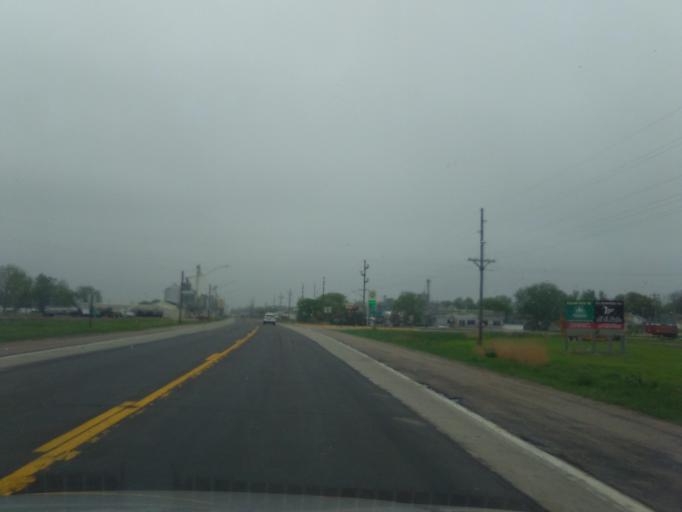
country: US
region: Nebraska
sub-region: Cuming County
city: Wisner
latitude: 41.9251
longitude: -96.8059
